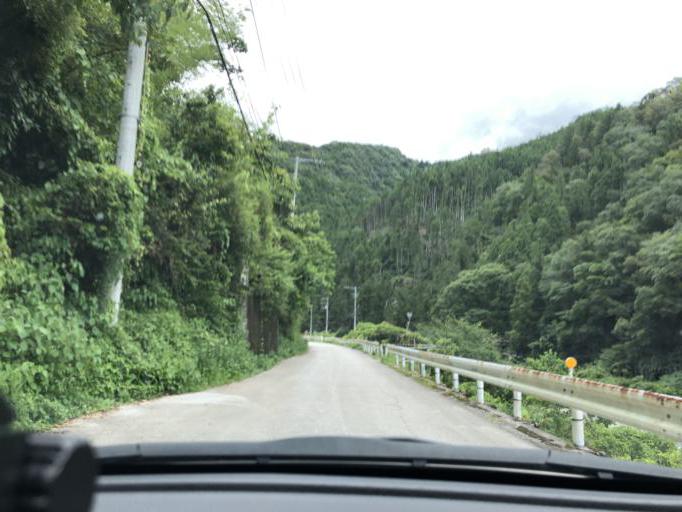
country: JP
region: Kochi
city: Kochi-shi
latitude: 33.6255
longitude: 133.5019
